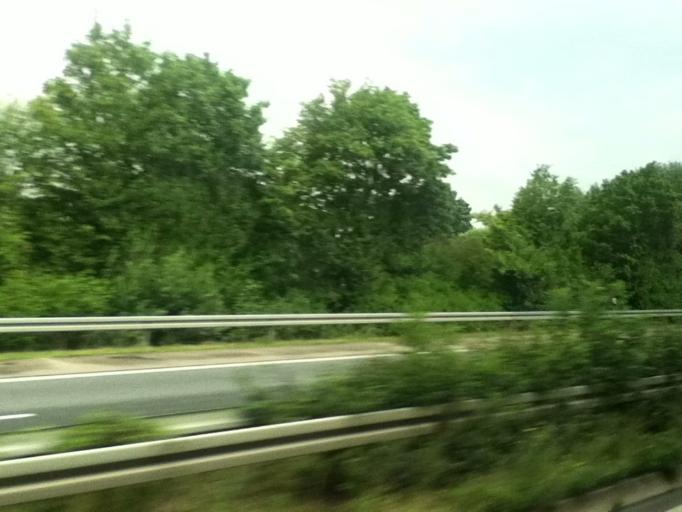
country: DE
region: Hesse
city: Allendorf an der Lahn
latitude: 50.5665
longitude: 8.5878
